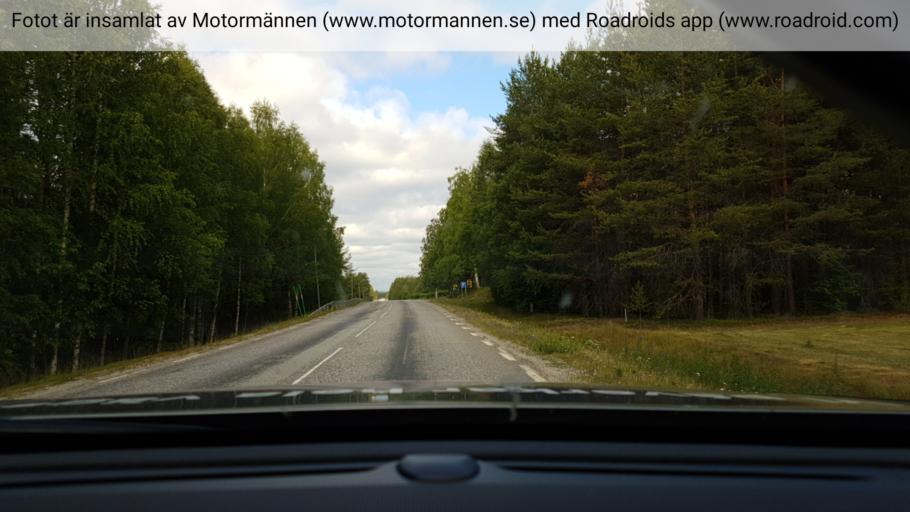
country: SE
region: Vaesterbotten
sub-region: Lycksele Kommun
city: Lycksele
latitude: 64.8202
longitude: 18.8421
